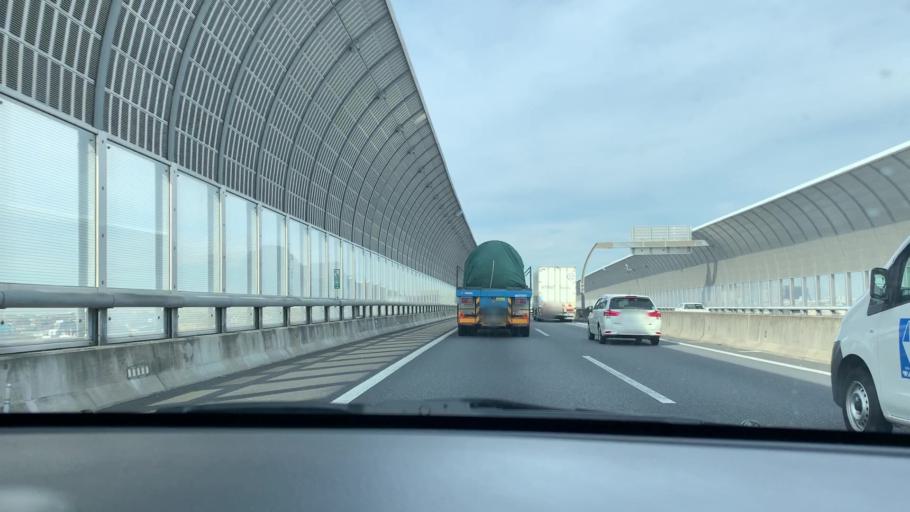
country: JP
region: Chiba
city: Matsudo
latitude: 35.8073
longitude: 139.8763
